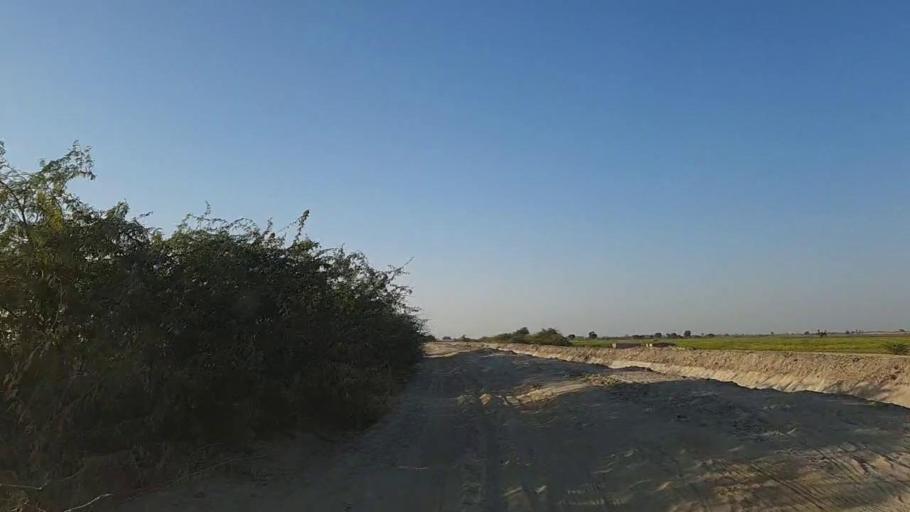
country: PK
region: Sindh
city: Naukot
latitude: 24.9986
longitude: 69.3988
